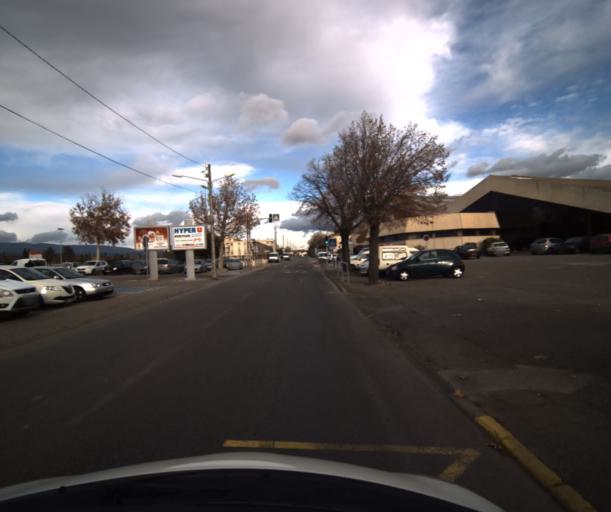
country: FR
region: Provence-Alpes-Cote d'Azur
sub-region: Departement du Vaucluse
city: Pertuis
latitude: 43.6947
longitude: 5.5105
